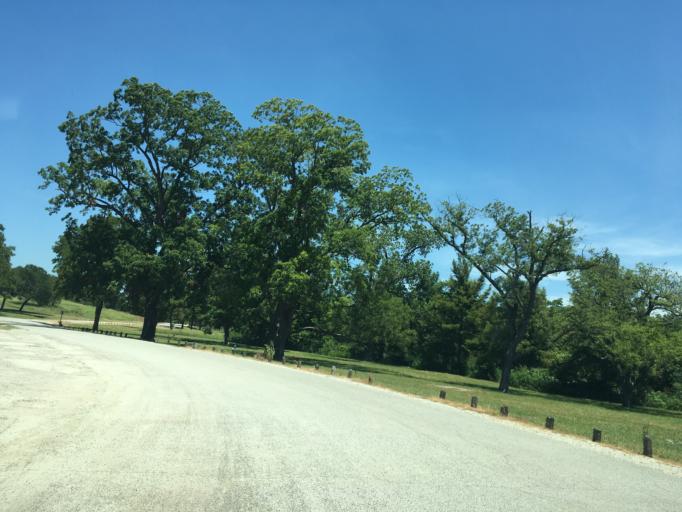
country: US
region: Texas
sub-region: Dallas County
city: Highland Park
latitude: 32.8355
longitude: -96.7145
